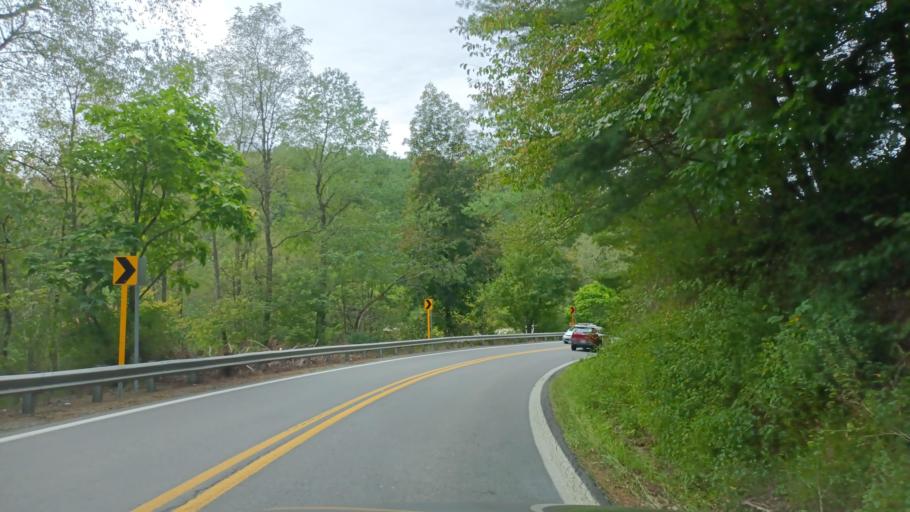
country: US
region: West Virginia
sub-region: Taylor County
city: Grafton
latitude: 39.3337
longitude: -79.8676
